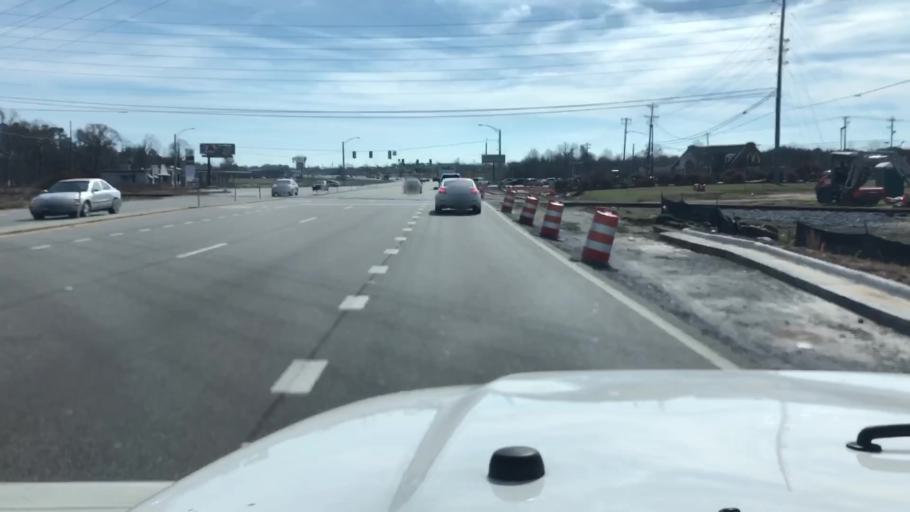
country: US
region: Alabama
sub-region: Montgomery County
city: Pike Road
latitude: 32.3642
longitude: -86.1371
